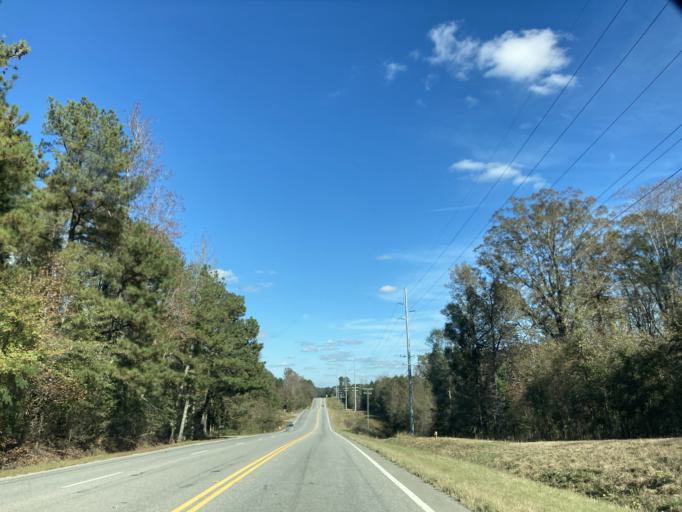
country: US
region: Georgia
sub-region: Jones County
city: Gray
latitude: 32.9238
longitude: -83.5092
